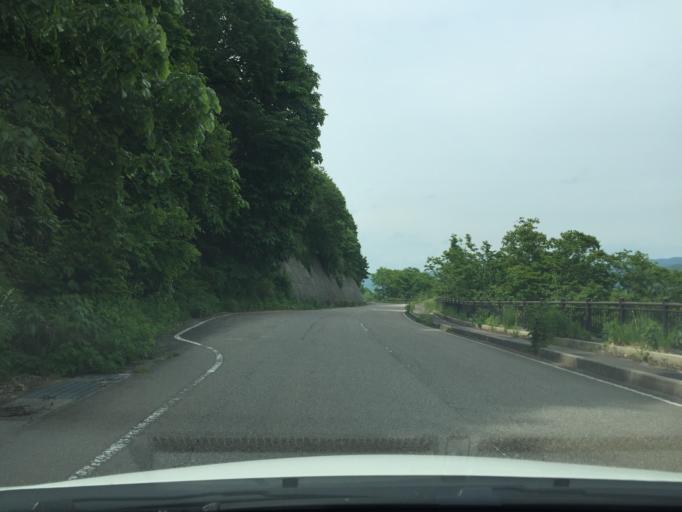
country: JP
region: Fukushima
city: Inawashiro
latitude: 37.6907
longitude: 140.0515
